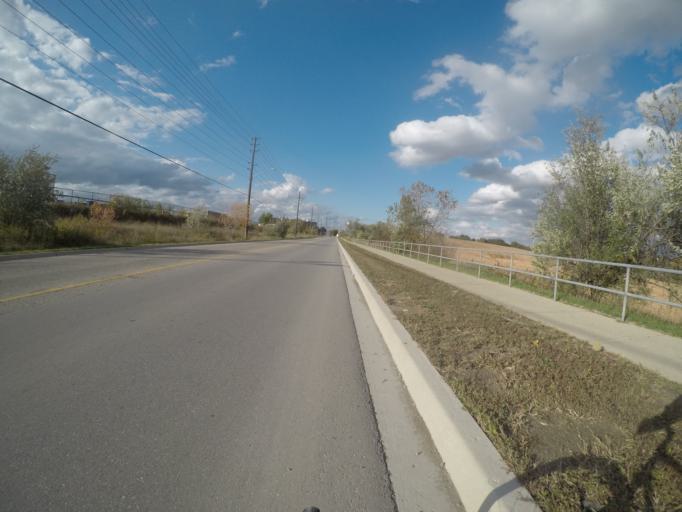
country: CA
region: Ontario
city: Kitchener
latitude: 43.4188
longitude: -80.4346
